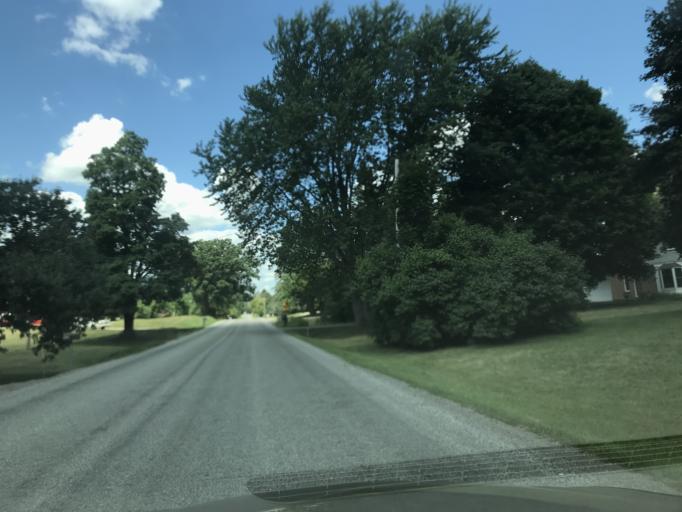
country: US
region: Michigan
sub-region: Ingham County
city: Holt
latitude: 42.6093
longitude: -84.5625
